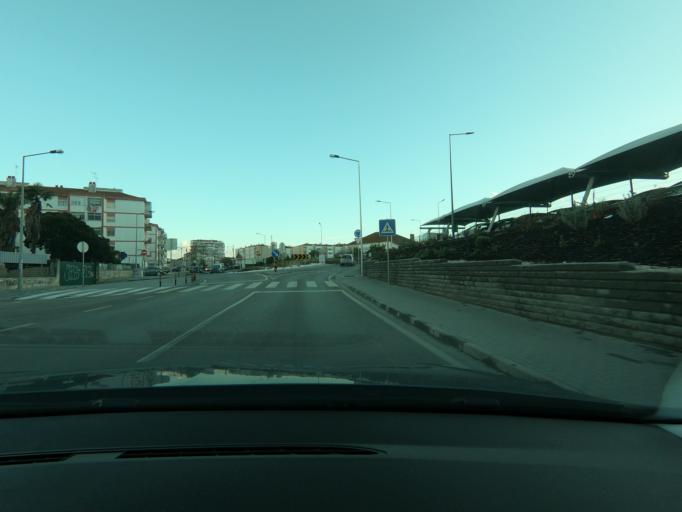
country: PT
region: Lisbon
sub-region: Alenquer
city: Carregado
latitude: 39.0267
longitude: -8.9801
